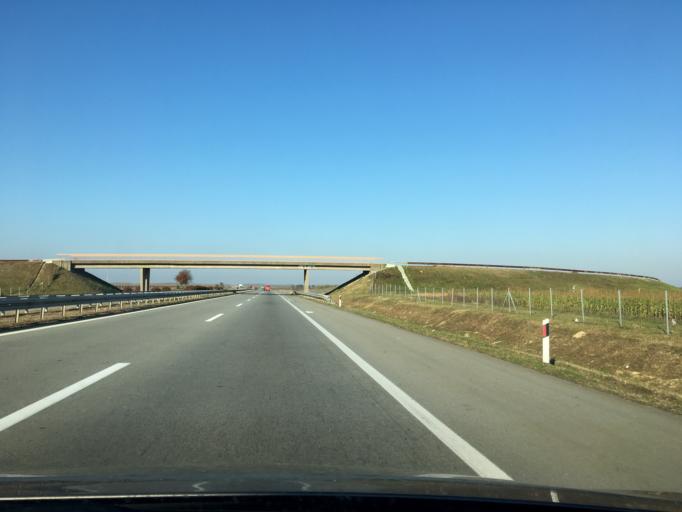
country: RS
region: Autonomna Pokrajina Vojvodina
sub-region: Juznobacki Okrug
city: Kovilj
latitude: 45.2583
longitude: 19.9992
